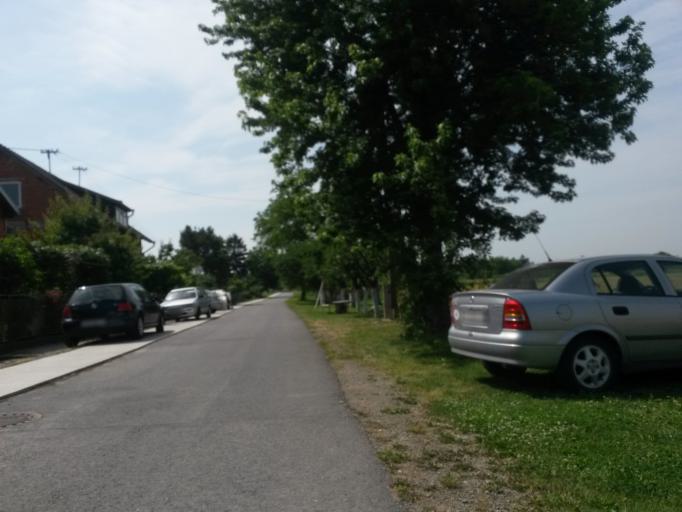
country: HR
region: Osjecko-Baranjska
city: Brijest
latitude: 45.5405
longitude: 18.6630
